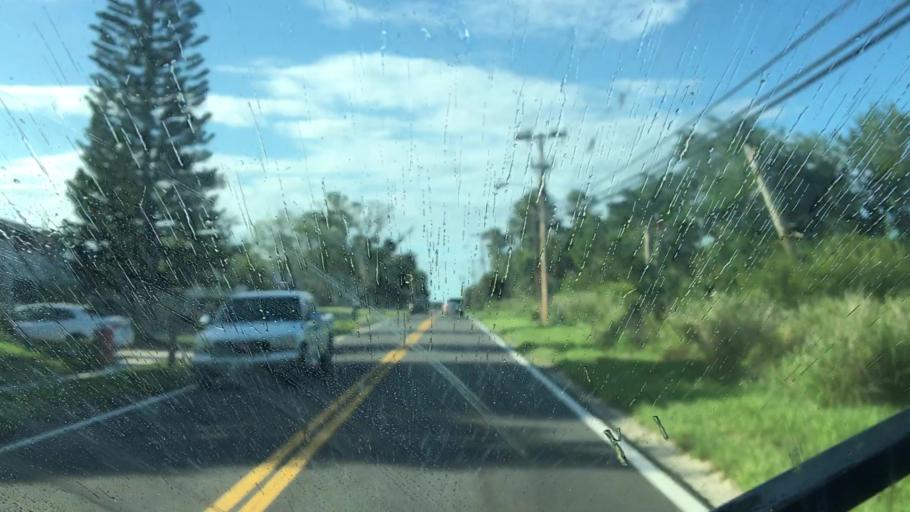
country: US
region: Florida
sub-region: Brevard County
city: Mims
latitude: 28.6222
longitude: -80.8603
